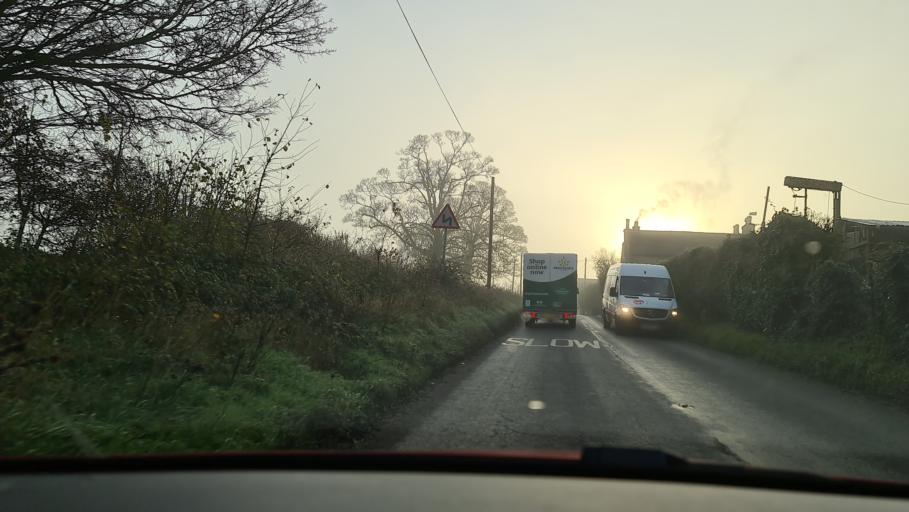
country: GB
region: England
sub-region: Buckinghamshire
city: Haddenham
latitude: 51.7941
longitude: -0.9402
